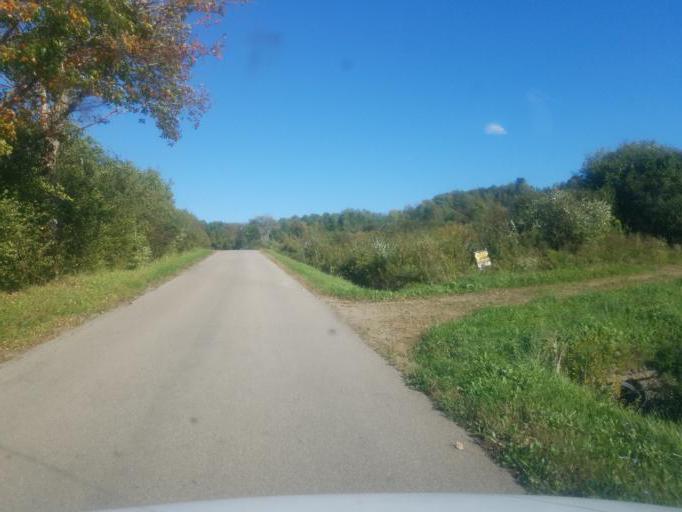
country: US
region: New York
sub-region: Allegany County
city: Cuba
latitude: 42.2340
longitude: -78.2373
